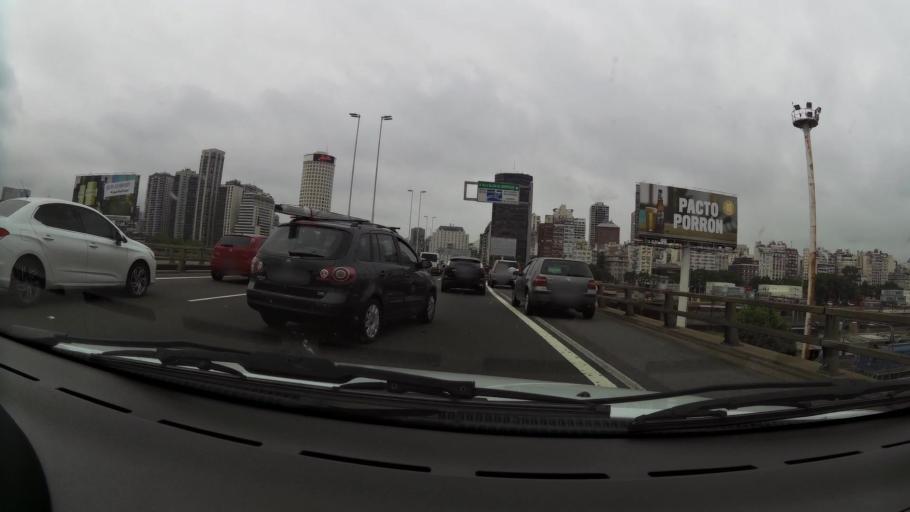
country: AR
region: Buenos Aires F.D.
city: Retiro
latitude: -34.5859
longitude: -58.3803
